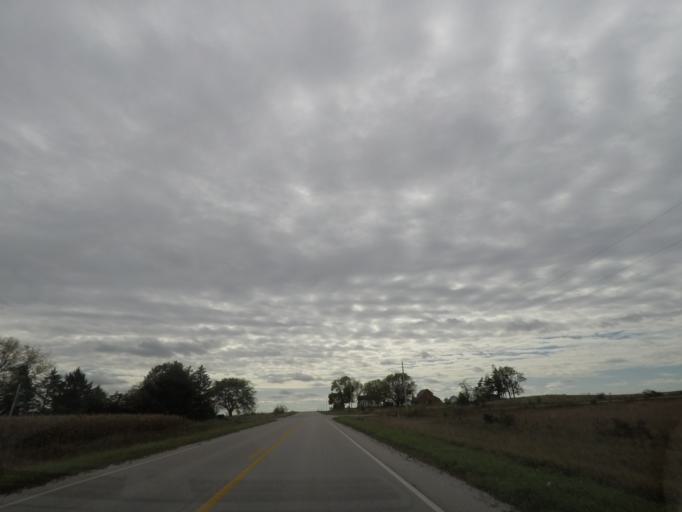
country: US
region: Iowa
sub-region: Story County
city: Huxley
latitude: 41.8639
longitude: -93.5317
